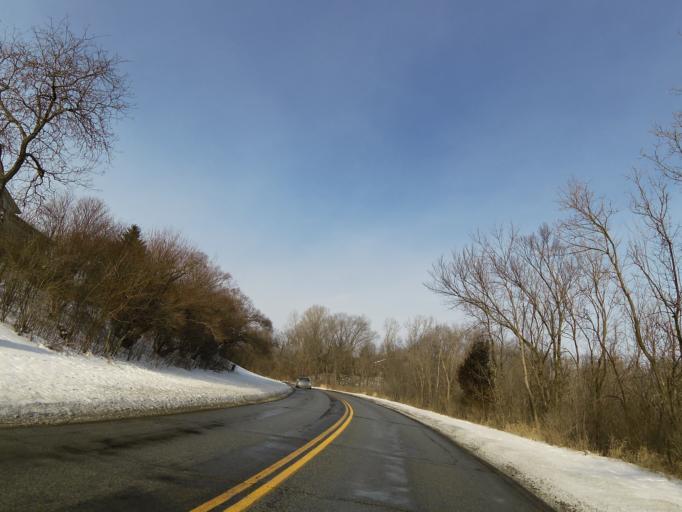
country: US
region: Minnesota
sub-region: Hennepin County
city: Eden Prairie
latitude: 44.8405
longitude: -93.4101
